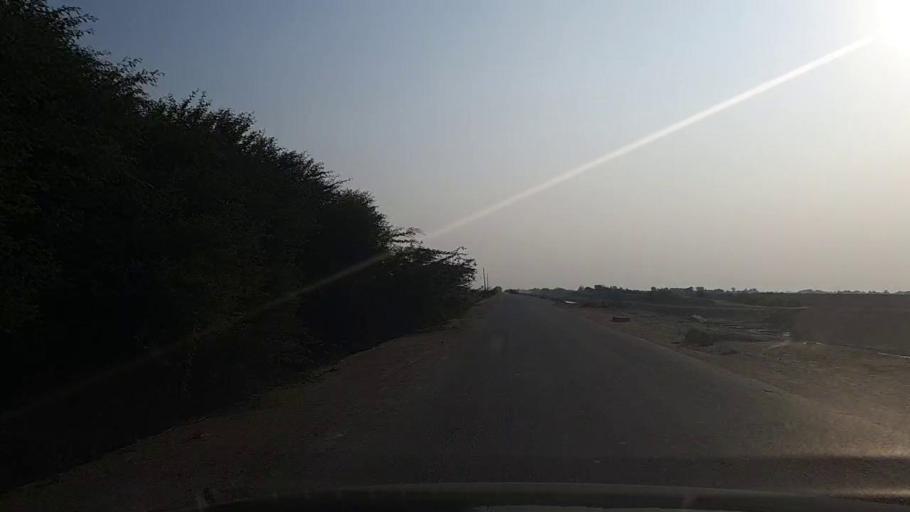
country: PK
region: Sindh
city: Mirpur Sakro
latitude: 24.5105
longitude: 67.8186
